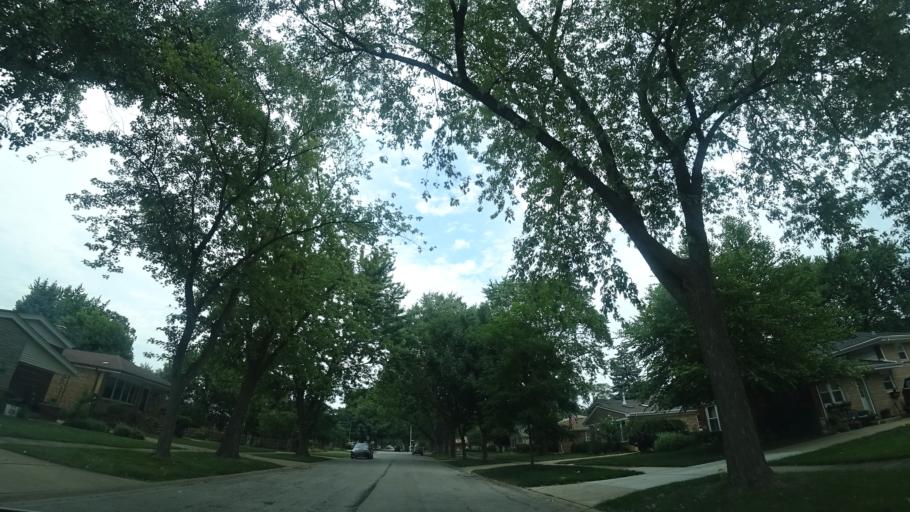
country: US
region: Illinois
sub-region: Cook County
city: Oak Lawn
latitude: 41.7011
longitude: -87.7291
